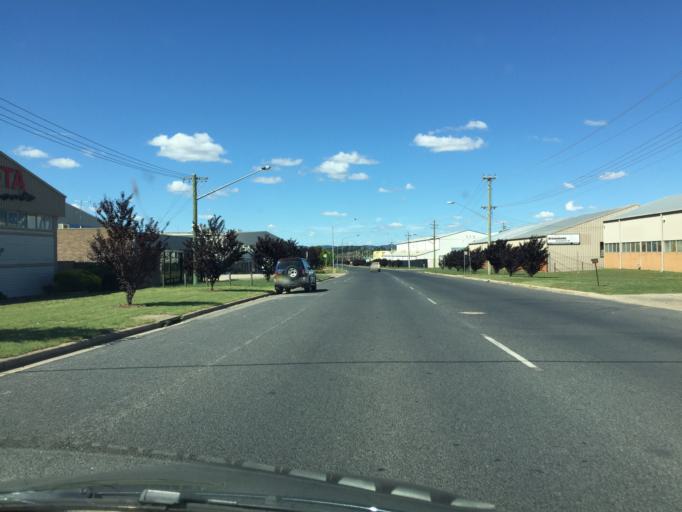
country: AU
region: Australian Capital Territory
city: Macarthur
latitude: -35.3893
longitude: 149.1696
